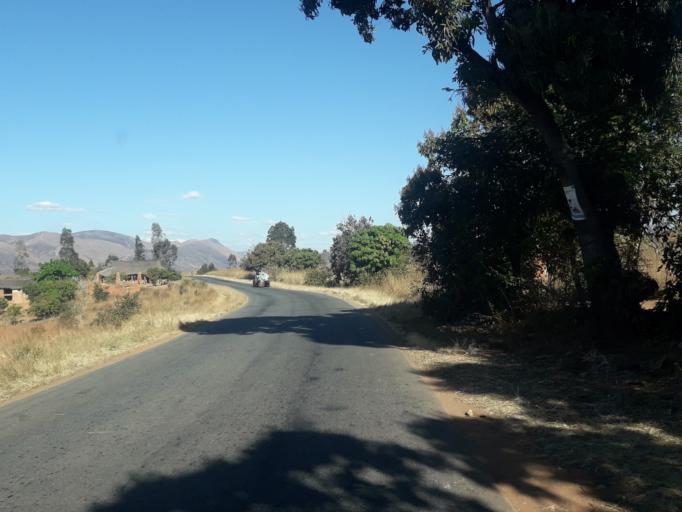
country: MG
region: Analamanga
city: Ankazobe
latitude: -17.7278
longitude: 47.0035
